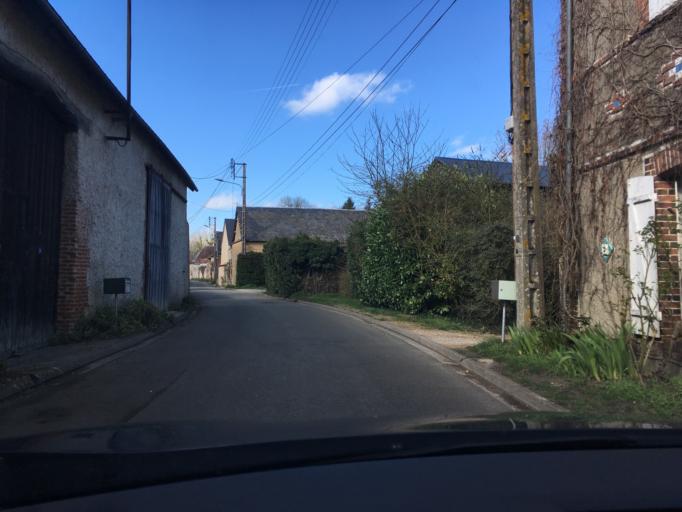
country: FR
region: Centre
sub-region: Departement d'Eure-et-Loir
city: Armenonville-les-Gatineaux
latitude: 48.5479
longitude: 1.6387
